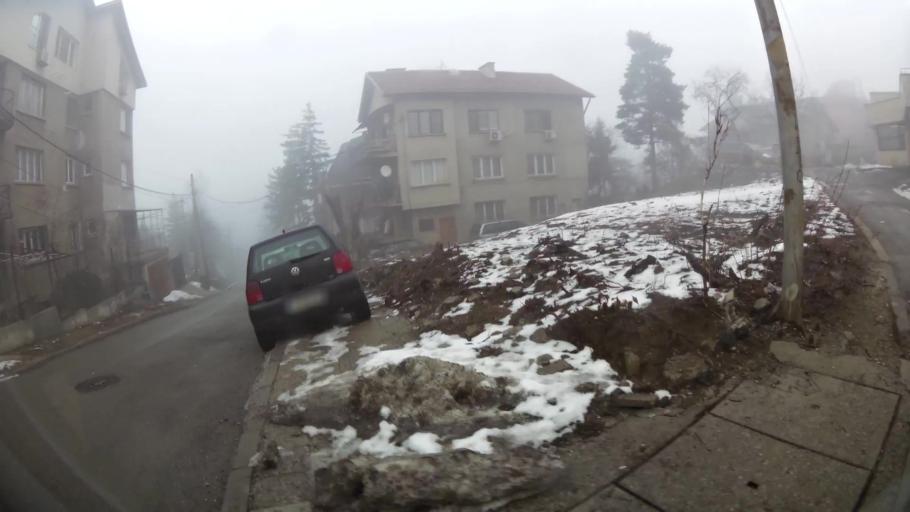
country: BG
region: Sofia-Capital
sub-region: Stolichna Obshtina
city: Sofia
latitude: 42.6608
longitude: 23.2598
